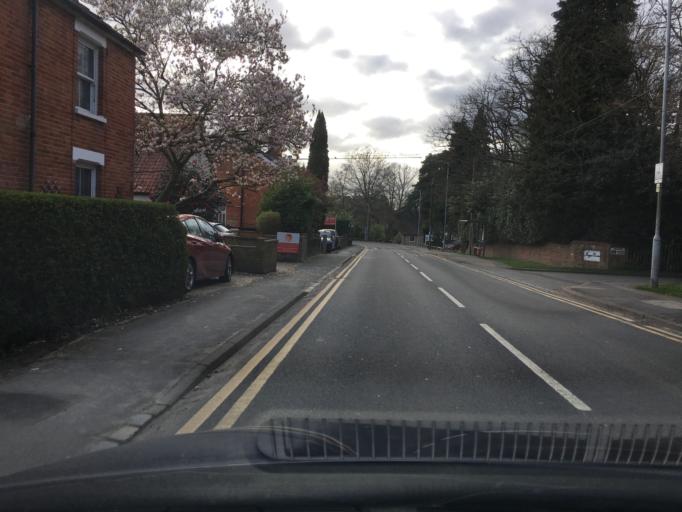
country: GB
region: England
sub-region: Bracknell Forest
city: Crowthorne
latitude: 51.3707
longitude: -0.7952
